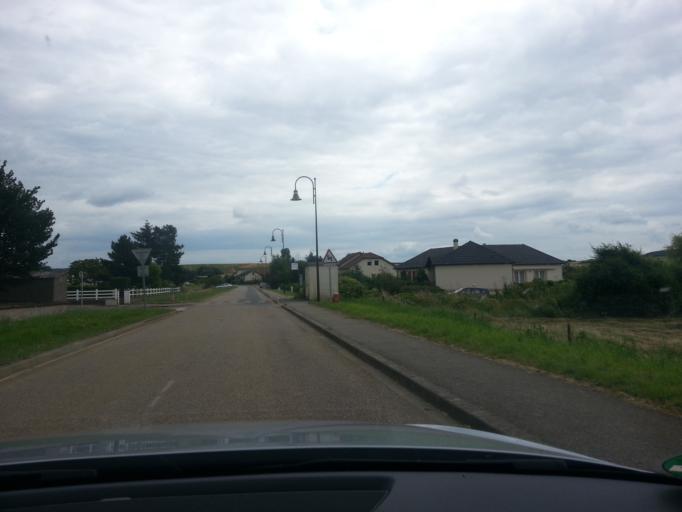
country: LU
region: Grevenmacher
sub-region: Canton de Remich
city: Mondorf-les-Bains
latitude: 49.4727
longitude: 6.2905
